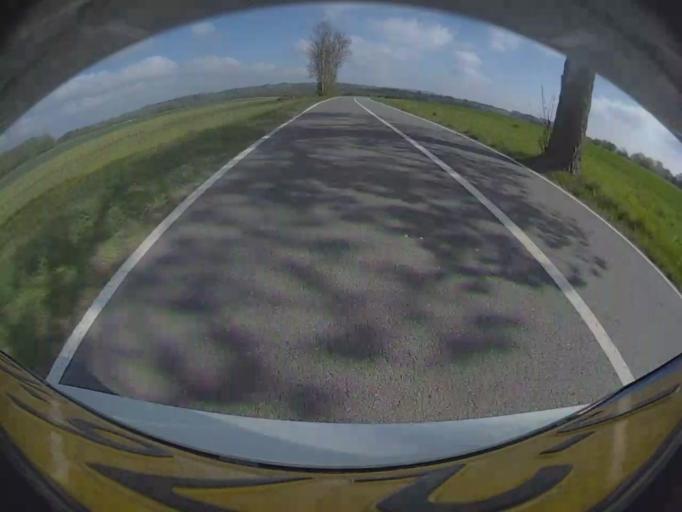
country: BE
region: Wallonia
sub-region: Province du Luxembourg
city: Tellin
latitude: 50.1055
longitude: 5.2336
